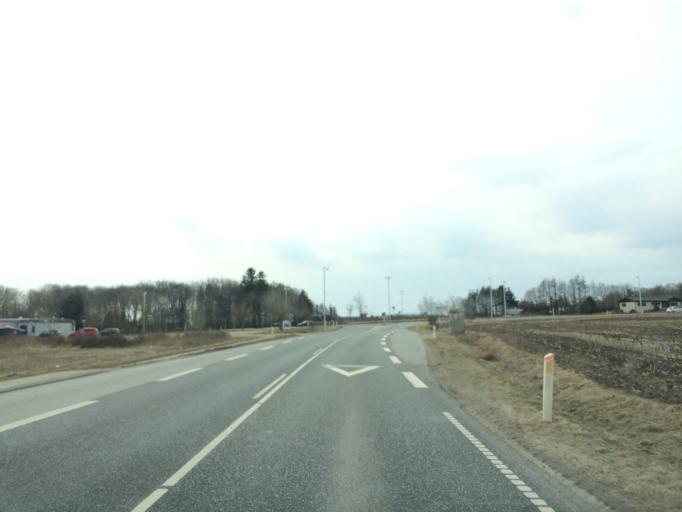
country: DK
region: Central Jutland
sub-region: Ringkobing-Skjern Kommune
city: Videbaek
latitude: 56.0873
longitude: 8.5073
